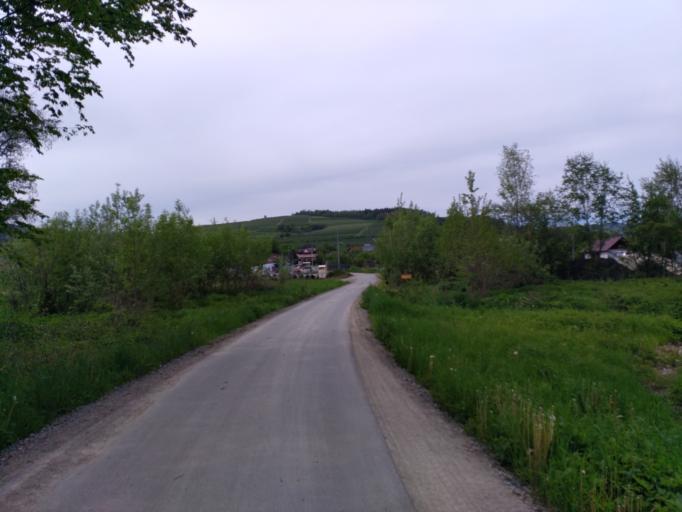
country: PL
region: Lesser Poland Voivodeship
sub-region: Powiat nowosadecki
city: Lacko
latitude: 49.5515
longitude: 20.4298
